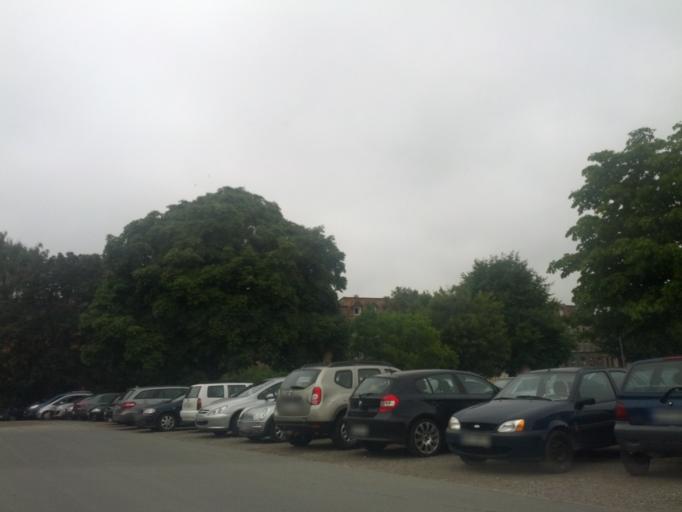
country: DE
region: Mecklenburg-Vorpommern
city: Wismar
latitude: 53.8900
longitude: 11.4696
